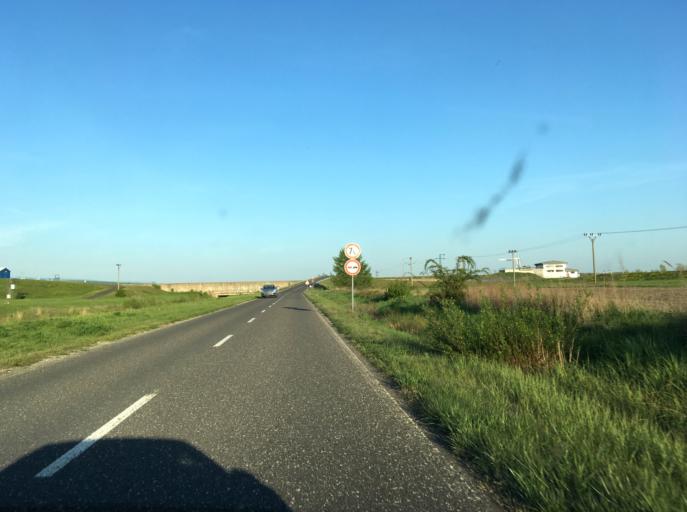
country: SK
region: Trnavsky
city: Samorin
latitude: 47.9926
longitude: 17.3489
